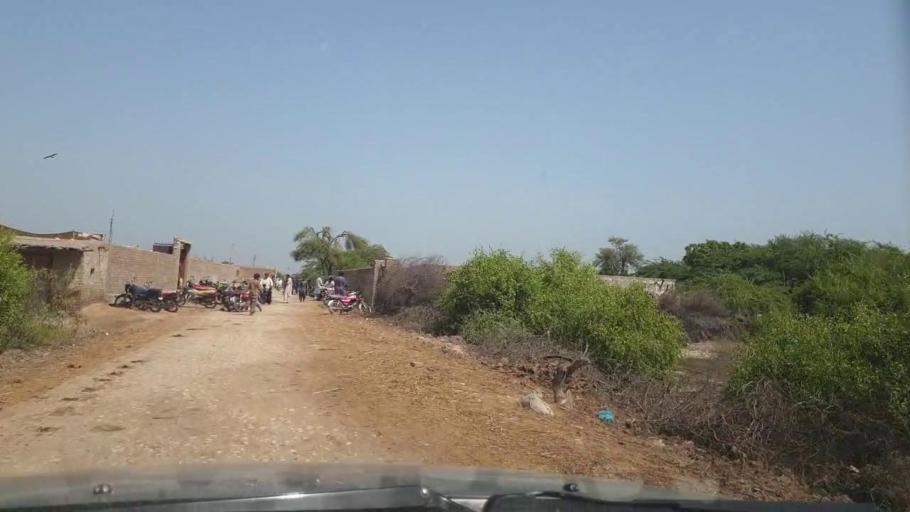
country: PK
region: Sindh
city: Tando Ghulam Ali
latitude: 25.1483
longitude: 68.7653
